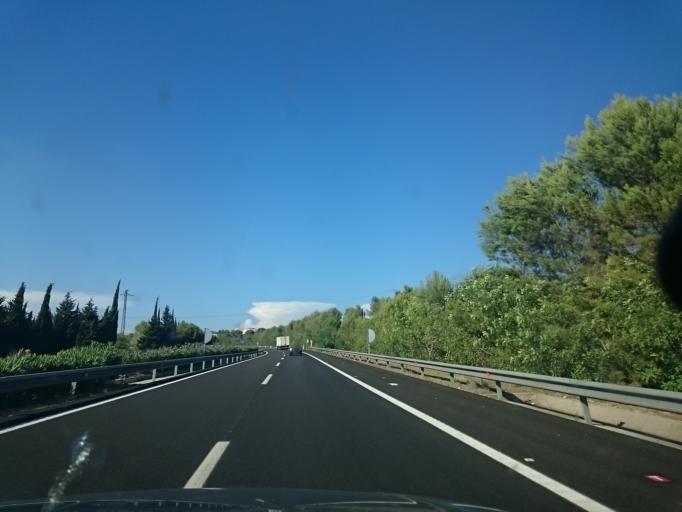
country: ES
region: Catalonia
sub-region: Provincia de Barcelona
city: Cubelles
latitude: 41.2318
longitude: 1.6796
